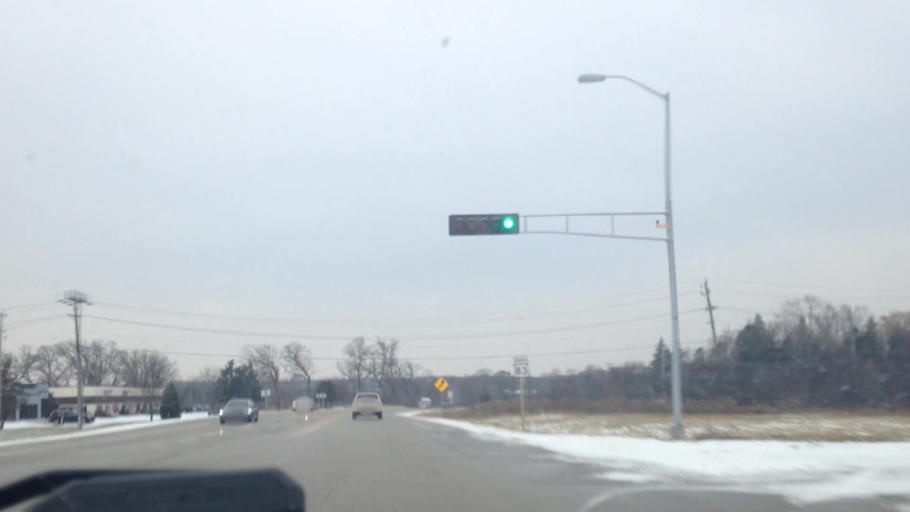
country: US
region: Wisconsin
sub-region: Waukesha County
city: Hartland
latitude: 43.0939
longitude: -88.3621
